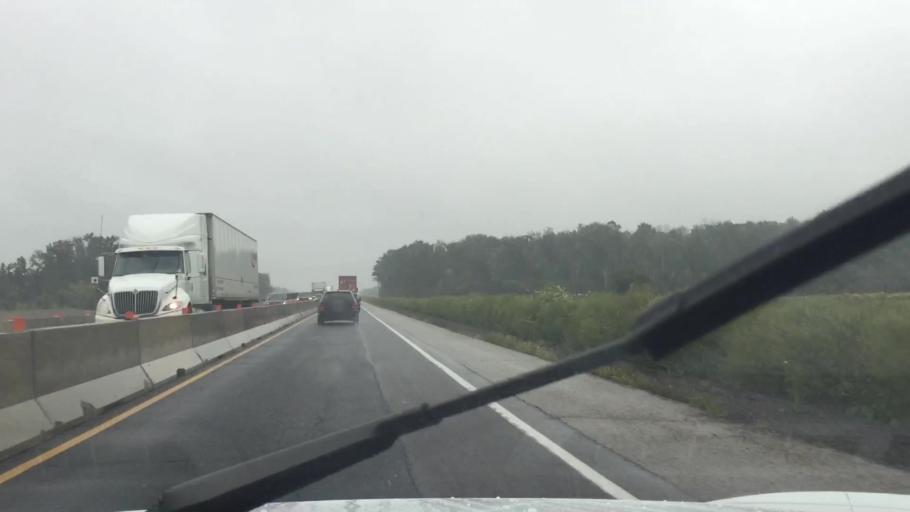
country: CA
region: Ontario
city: Delaware
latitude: 42.8115
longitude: -81.3226
